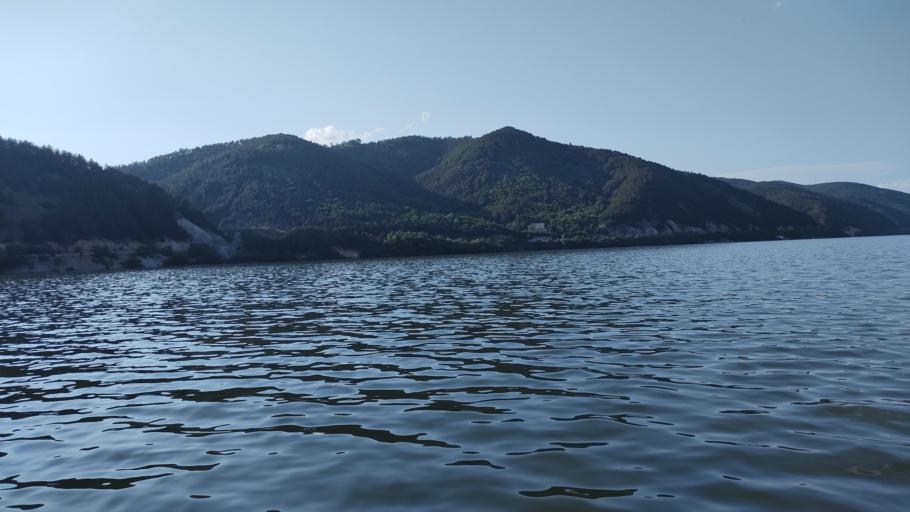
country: RO
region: Mehedinti
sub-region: Comuna Svinita
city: Svinita
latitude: 44.5127
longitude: 22.1994
